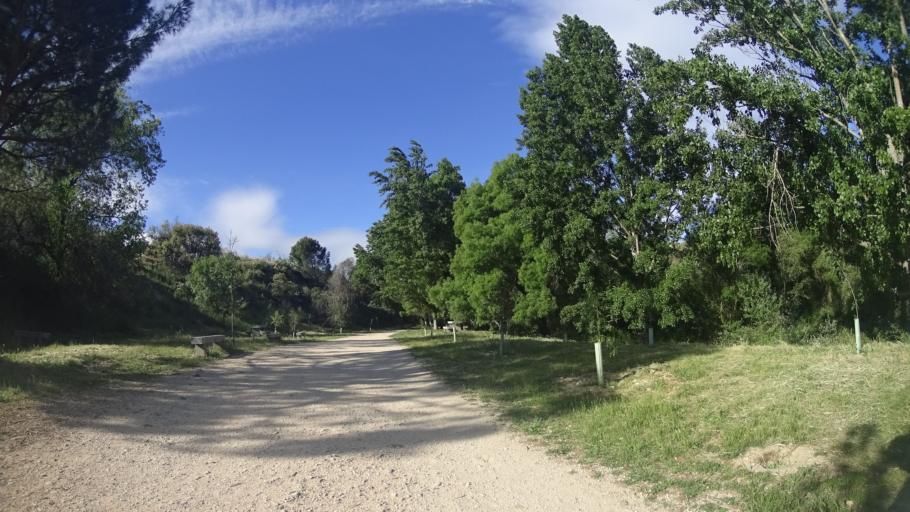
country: ES
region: Madrid
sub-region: Provincia de Madrid
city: Villanueva del Pardillo
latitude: 40.5188
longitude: -3.9393
